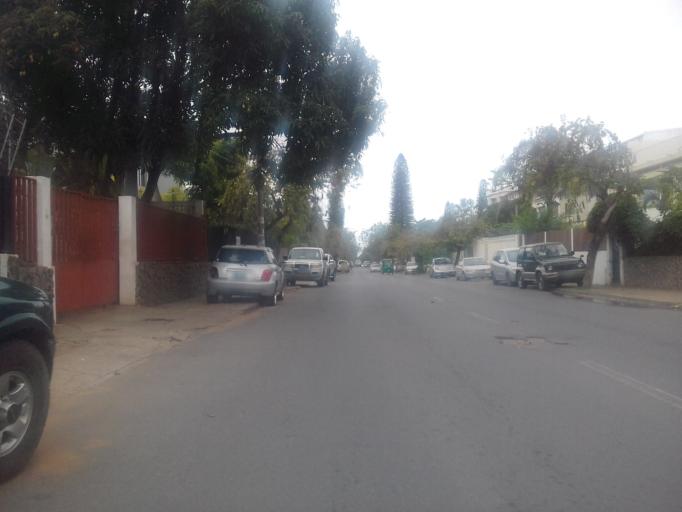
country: MZ
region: Maputo City
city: Maputo
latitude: -25.9565
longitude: 32.5966
